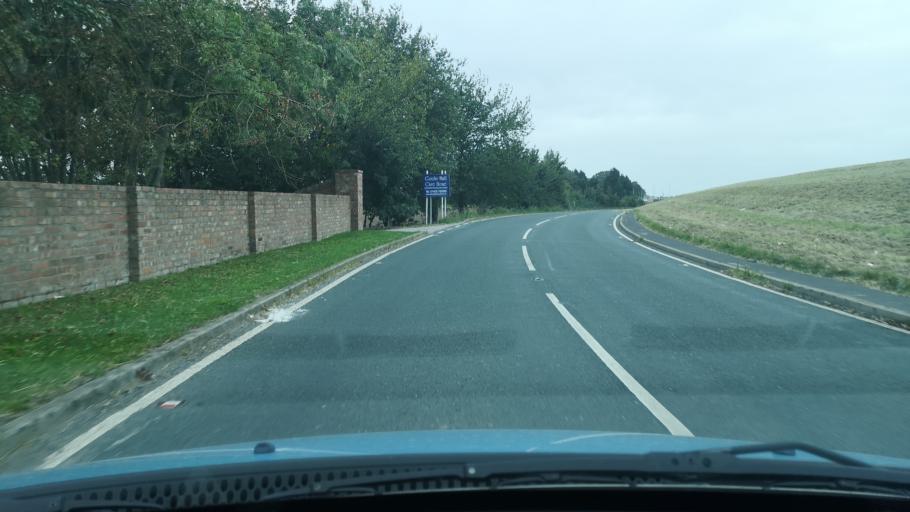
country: GB
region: England
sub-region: East Riding of Yorkshire
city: Goole
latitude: 53.6858
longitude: -0.8599
